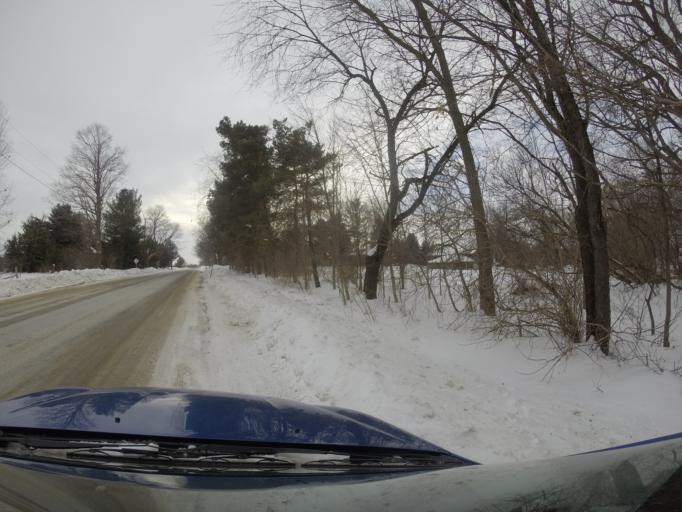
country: CA
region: Ontario
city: Wasaga Beach
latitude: 44.4221
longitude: -80.0629
